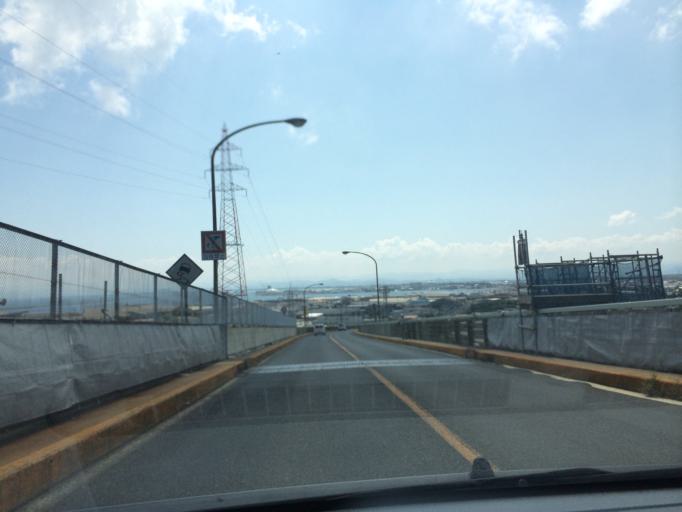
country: JP
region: Shimane
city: Sakaiminato
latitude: 35.5475
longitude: 133.2452
